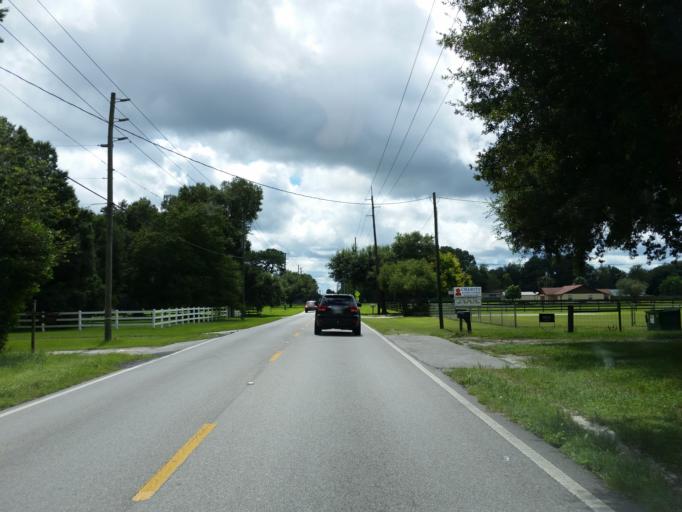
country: US
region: Florida
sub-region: Pasco County
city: Zephyrhills West
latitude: 28.2136
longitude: -82.2462
